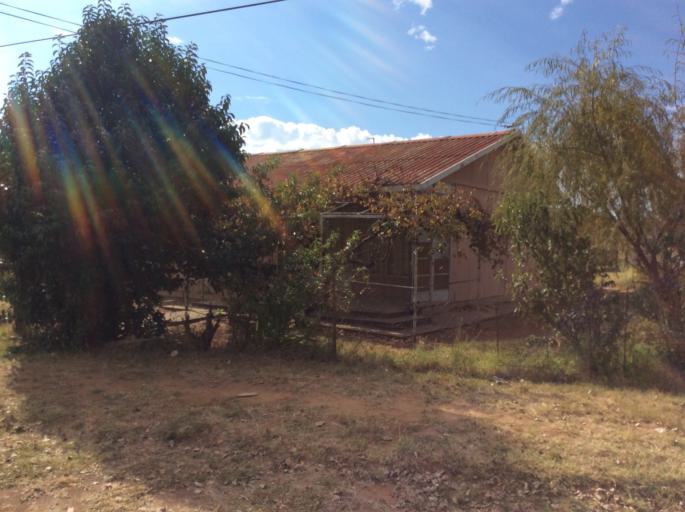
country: LS
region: Mafeteng
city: Mafeteng
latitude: -29.7298
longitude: 27.0251
